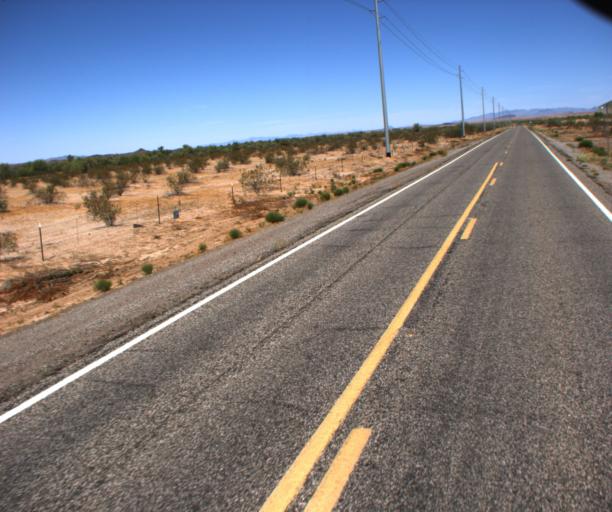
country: US
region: Arizona
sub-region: La Paz County
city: Cienega Springs
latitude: 33.9642
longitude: -114.0353
